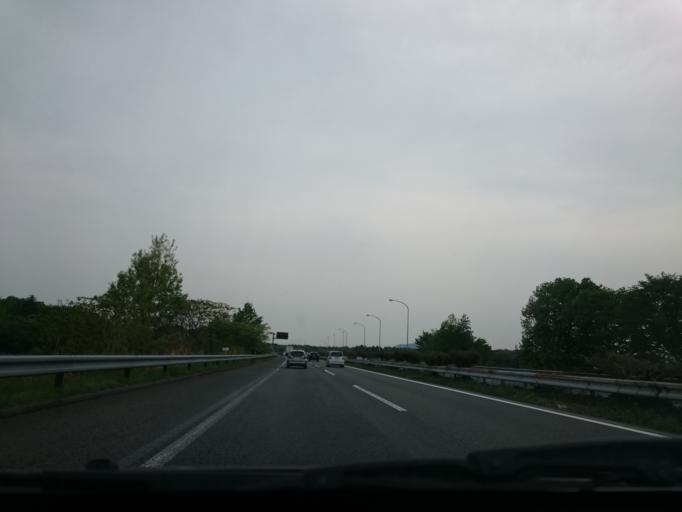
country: JP
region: Tochigi
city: Utsunomiya-shi
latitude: 36.6351
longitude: 139.8483
